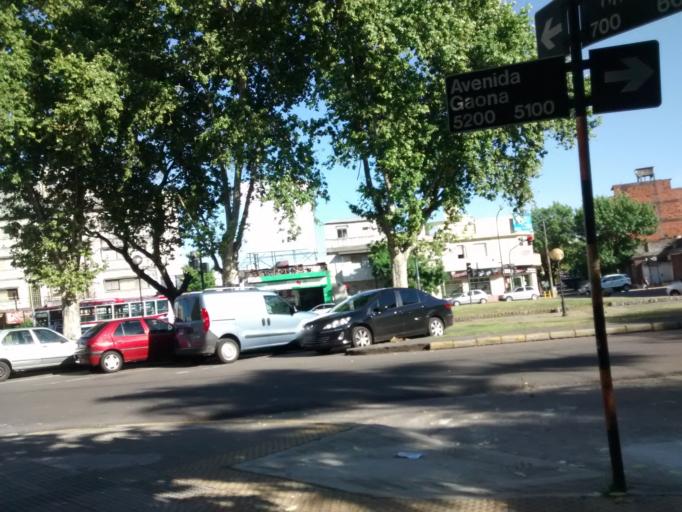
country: AR
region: Buenos Aires F.D.
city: Villa Santa Rita
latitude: -34.6293
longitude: -58.4935
